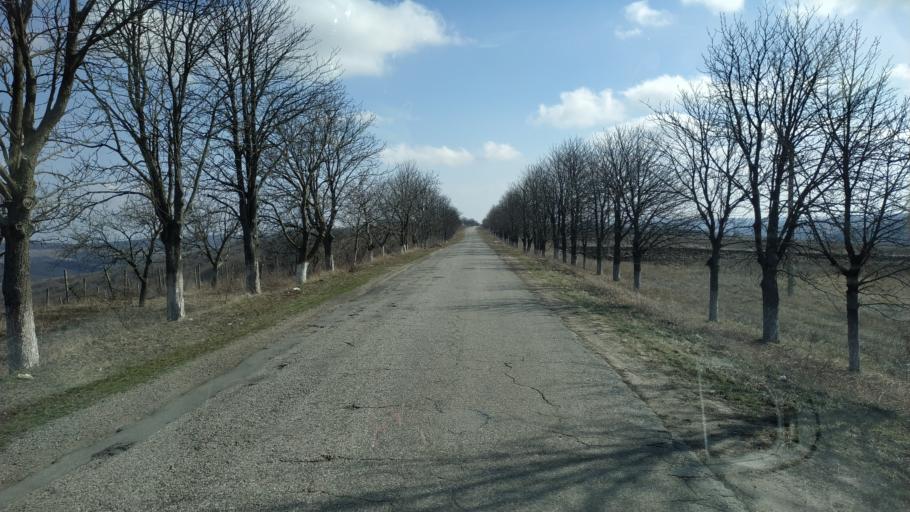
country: MD
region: Hincesti
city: Hincesti
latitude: 46.8538
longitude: 28.6426
